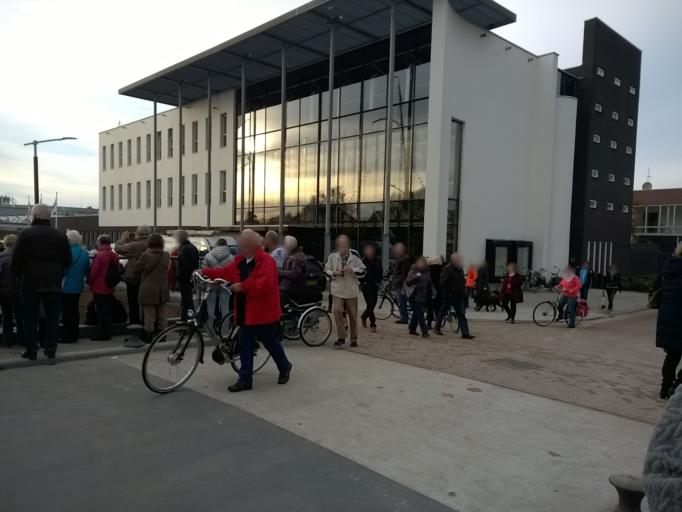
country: NL
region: Friesland
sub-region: Gemeente Smallingerland
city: Drachten
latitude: 53.1066
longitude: 6.0951
